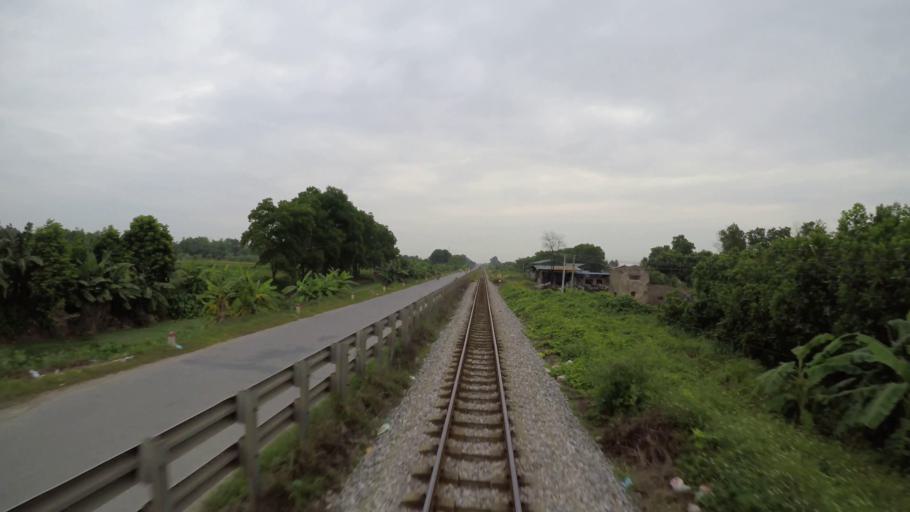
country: VN
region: Hung Yen
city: Ban Yen Nhan
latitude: 20.9853
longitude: 106.0621
